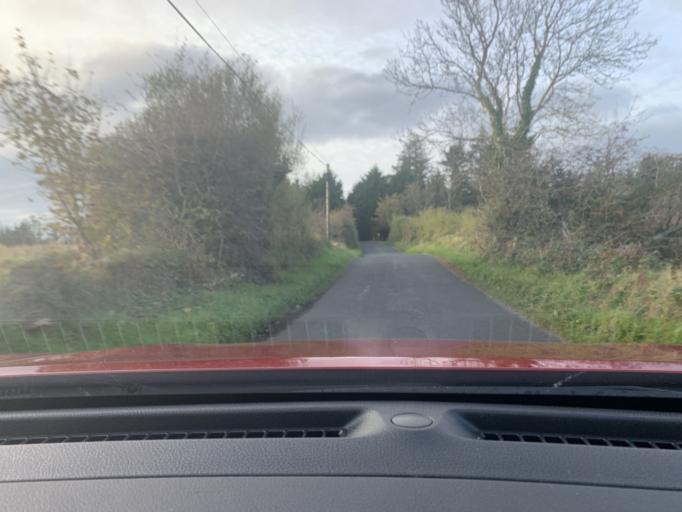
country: IE
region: Connaught
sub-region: Roscommon
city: Ballaghaderreen
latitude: 53.9131
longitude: -8.5868
